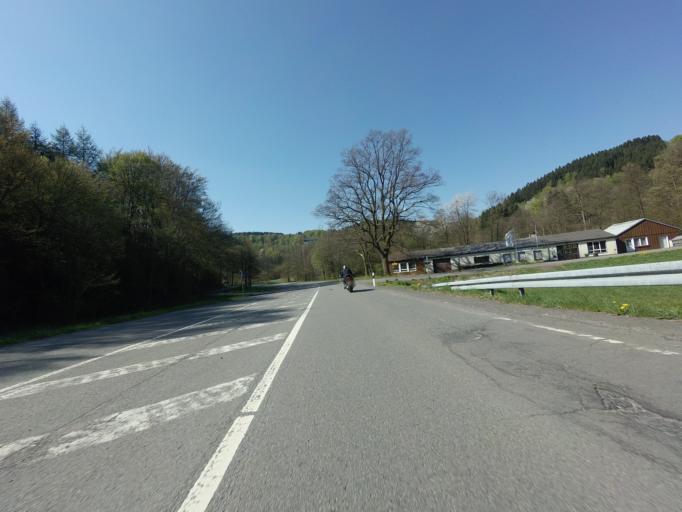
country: DE
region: North Rhine-Westphalia
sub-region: Regierungsbezirk Arnsberg
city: Herscheid
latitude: 51.1063
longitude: 7.7259
